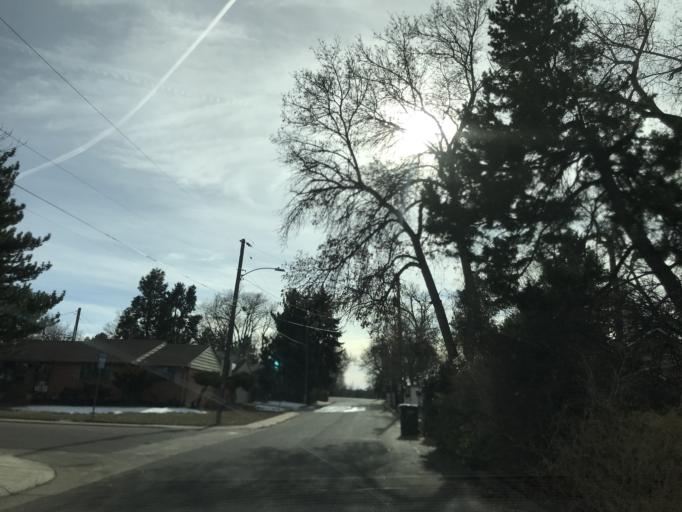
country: US
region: Colorado
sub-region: Arapahoe County
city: Littleton
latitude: 39.6004
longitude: -105.0140
